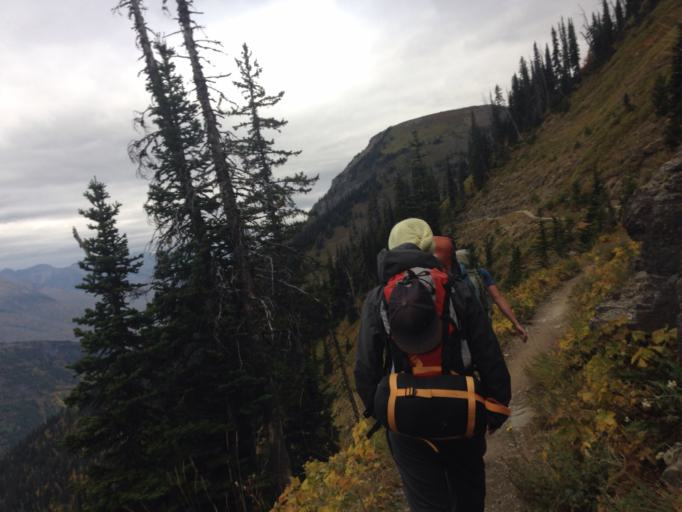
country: US
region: Montana
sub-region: Flathead County
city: Columbia Falls
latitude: 48.7209
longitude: -113.7202
